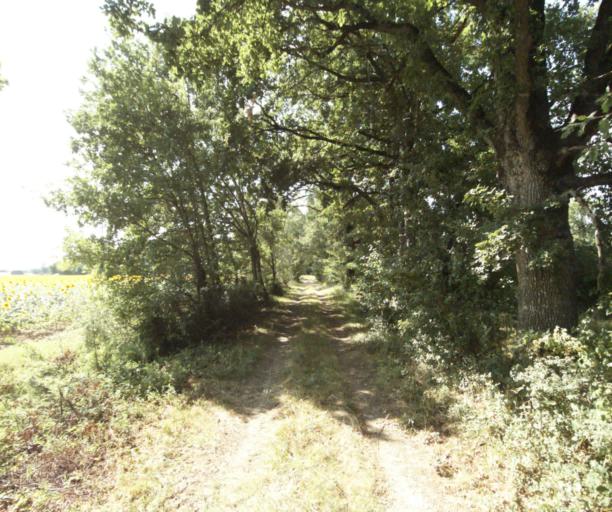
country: FR
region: Midi-Pyrenees
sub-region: Departement du Tarn
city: Soual
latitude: 43.5223
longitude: 2.0849
